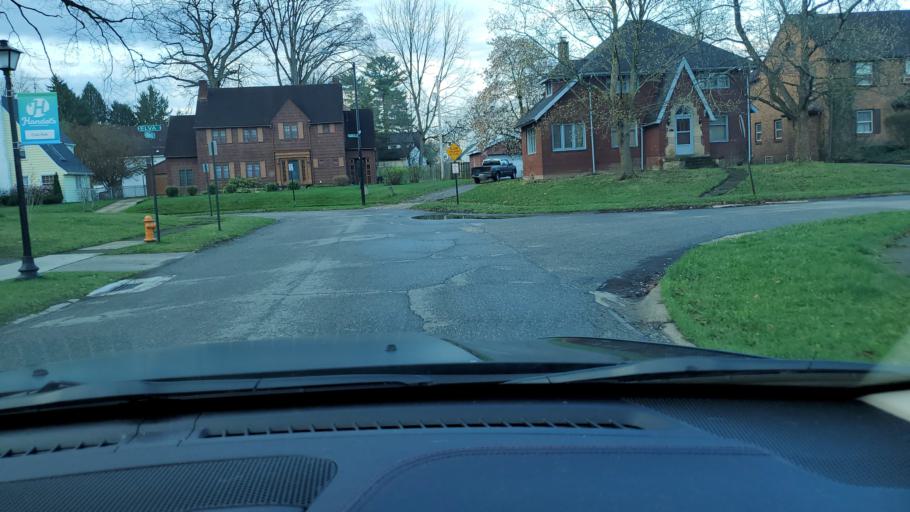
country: US
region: Ohio
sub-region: Mahoning County
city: Boardman
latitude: 41.0552
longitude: -80.6604
